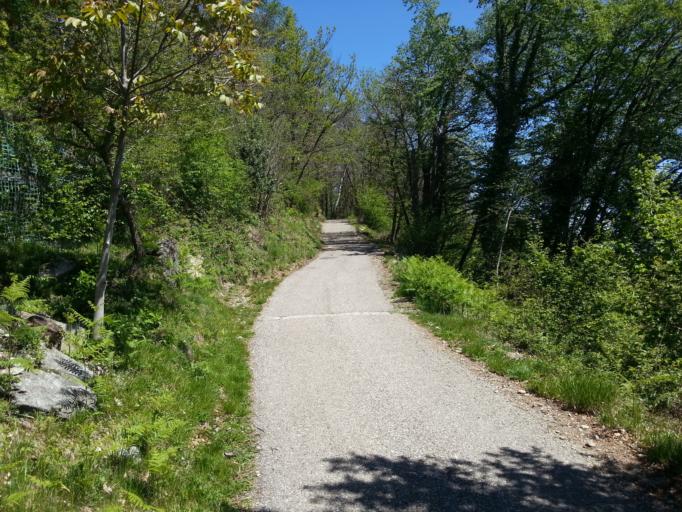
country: IT
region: Lombardy
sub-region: Provincia di Como
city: Plesio
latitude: 46.0447
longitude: 9.2197
